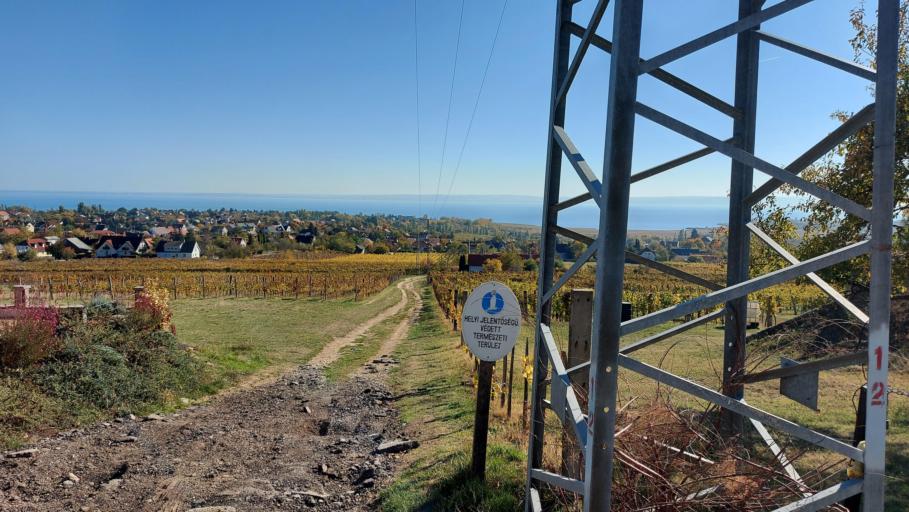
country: HU
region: Veszprem
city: Csopak
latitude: 46.9817
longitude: 17.9125
